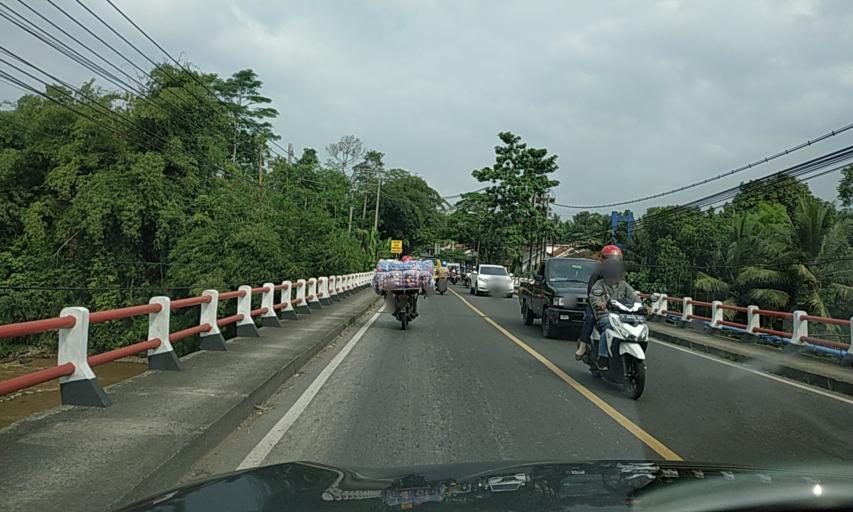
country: ID
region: Central Java
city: Purwokerto
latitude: -7.4183
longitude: 109.1933
